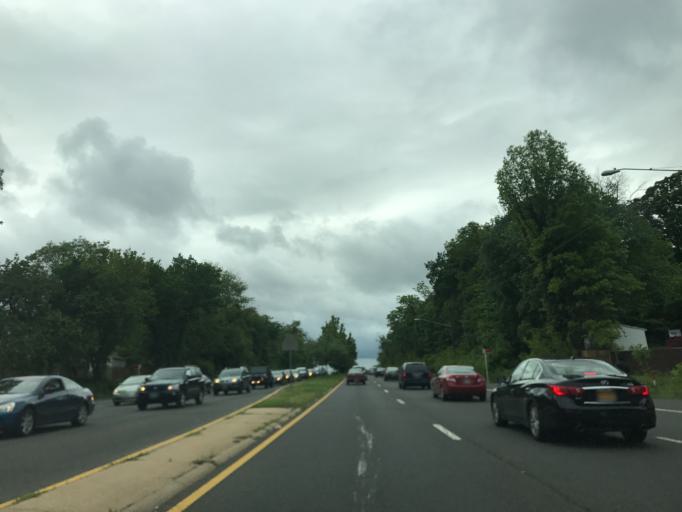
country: US
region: Maryland
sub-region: Prince George's County
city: Chillum
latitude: 38.9692
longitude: -76.9734
